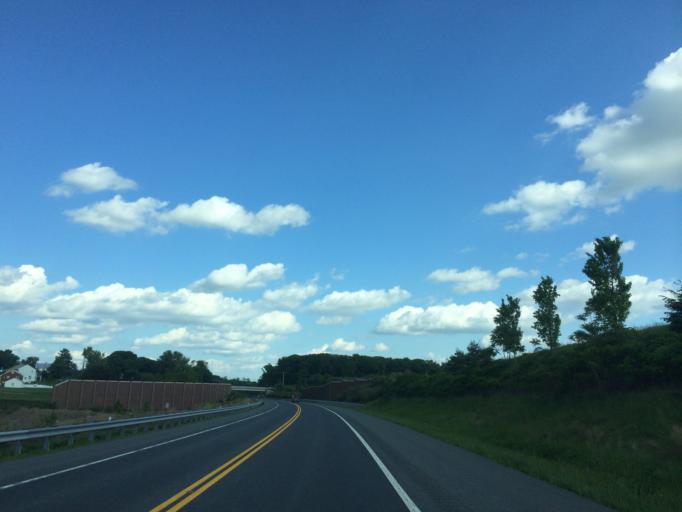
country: US
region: Maryland
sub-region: Carroll County
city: Hampstead
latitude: 39.5979
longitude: -76.8626
